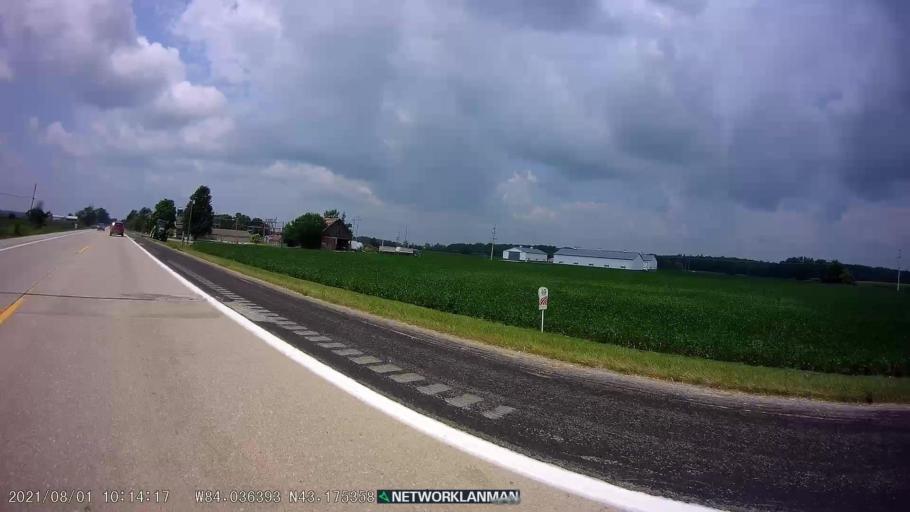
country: US
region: Michigan
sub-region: Saginaw County
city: Chesaning
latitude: 43.1754
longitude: -84.0368
